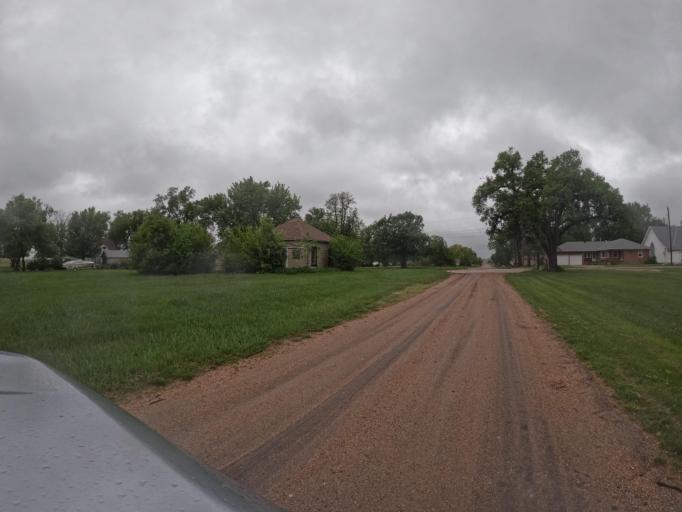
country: US
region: Nebraska
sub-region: Clay County
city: Harvard
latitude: 40.6144
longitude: -98.0953
